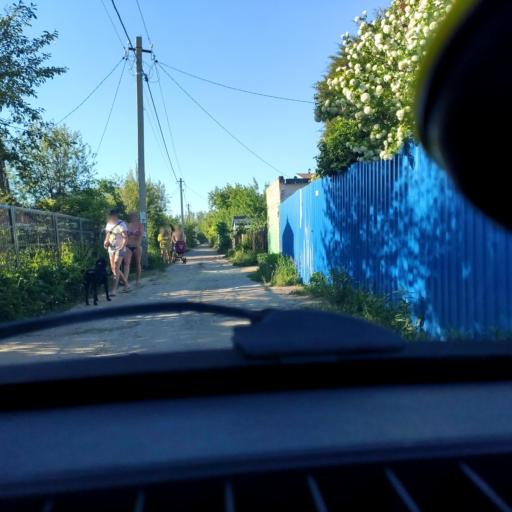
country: RU
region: Samara
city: Tol'yatti
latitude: 53.5954
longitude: 49.3149
